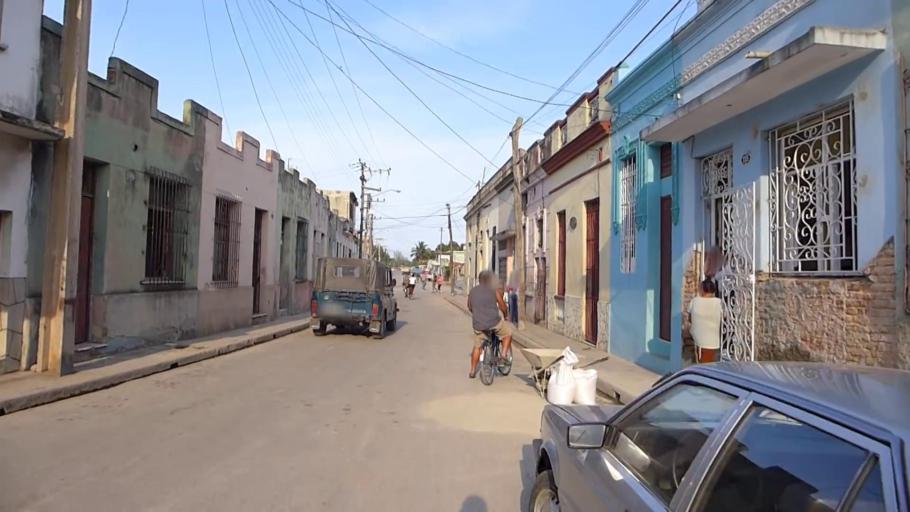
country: CU
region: Camaguey
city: Camaguey
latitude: 21.3840
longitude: -77.9086
